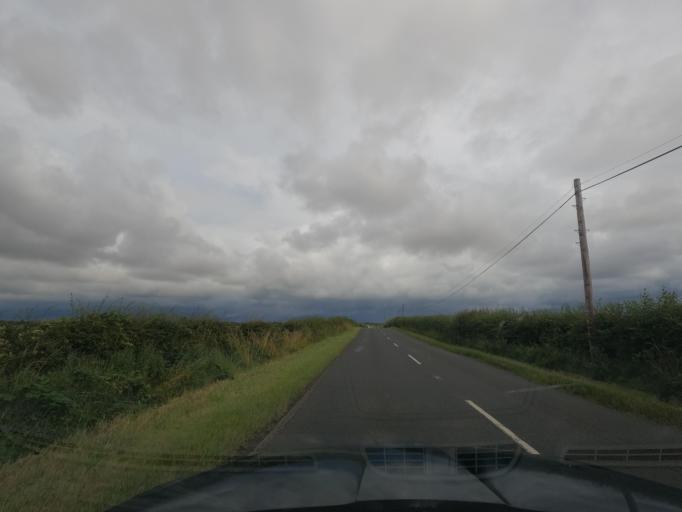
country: GB
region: England
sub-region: Northumberland
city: Ancroft
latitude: 55.6911
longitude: -2.0004
